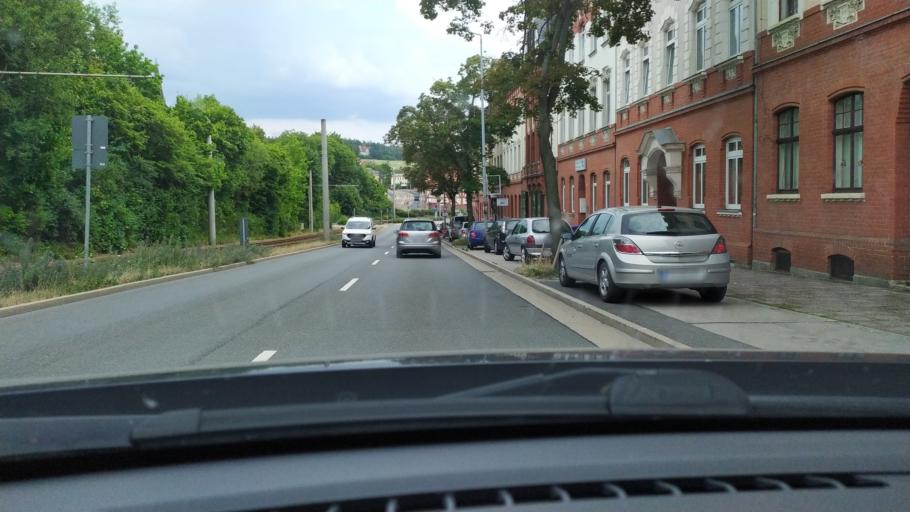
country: DE
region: Saxony
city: Plauen
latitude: 50.4949
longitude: 12.1533
